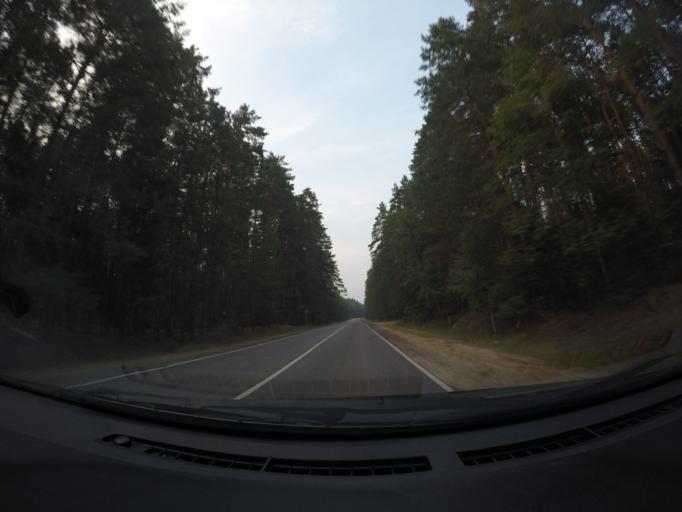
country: RU
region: Moskovskaya
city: Imeni Tsyurupy
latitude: 55.5070
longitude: 38.7155
